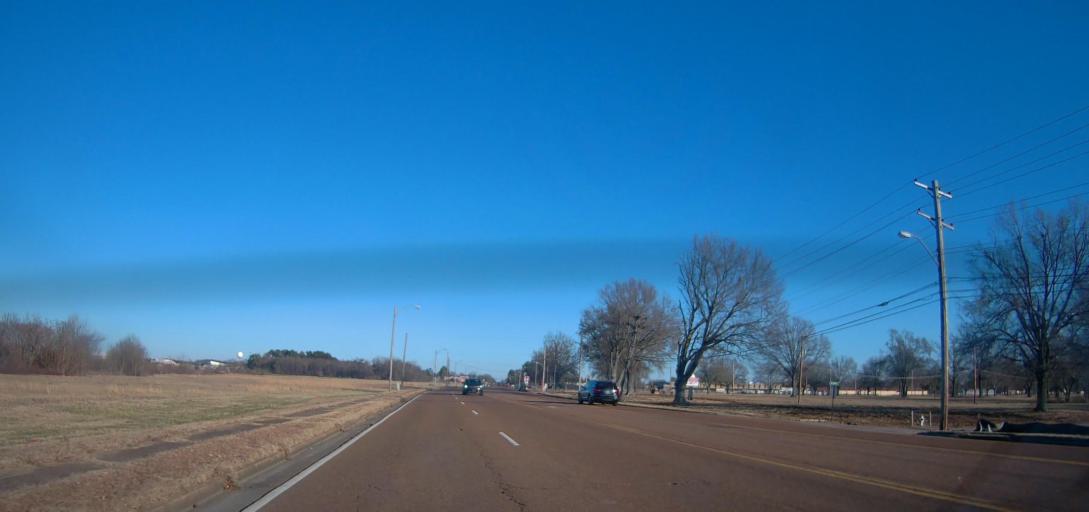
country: US
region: Tennessee
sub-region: Shelby County
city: Millington
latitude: 35.3414
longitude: -89.8872
